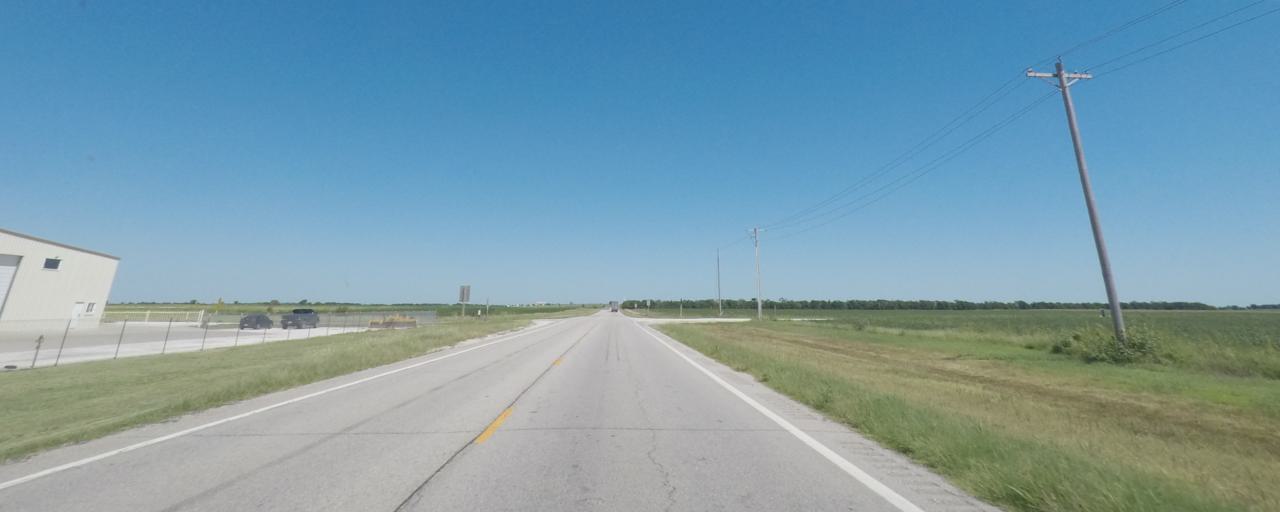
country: US
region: Kansas
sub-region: Sumner County
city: Wellington
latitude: 37.3322
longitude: -97.3849
